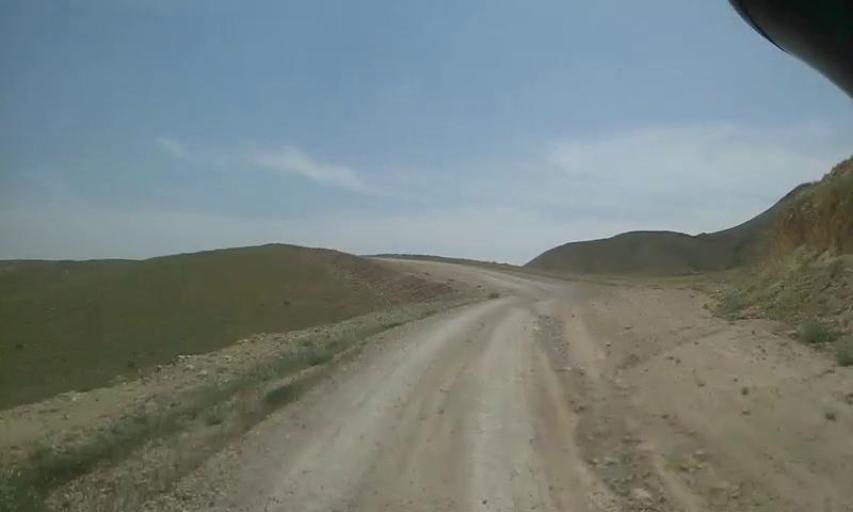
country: PS
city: `Arab ar Rashaydah
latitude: 31.5001
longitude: 35.2939
